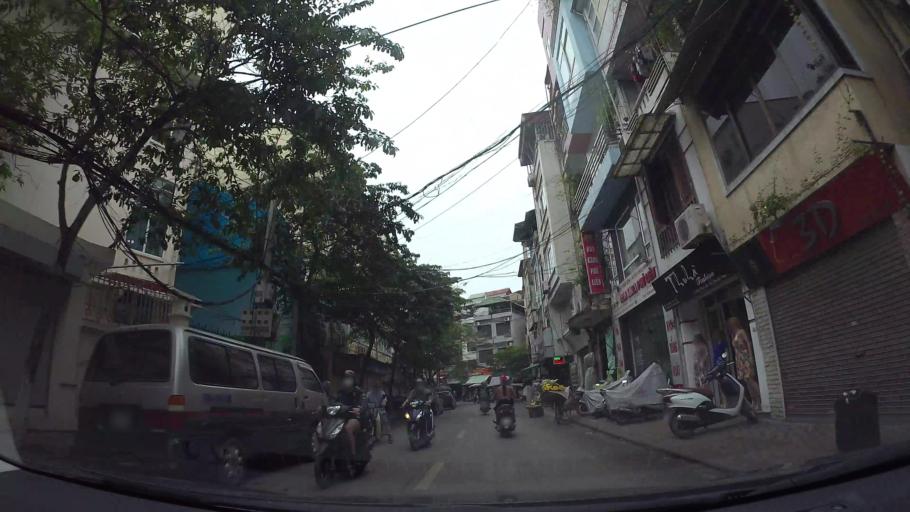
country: VN
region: Ha Noi
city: Hai BaTrung
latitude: 21.0123
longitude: 105.8607
